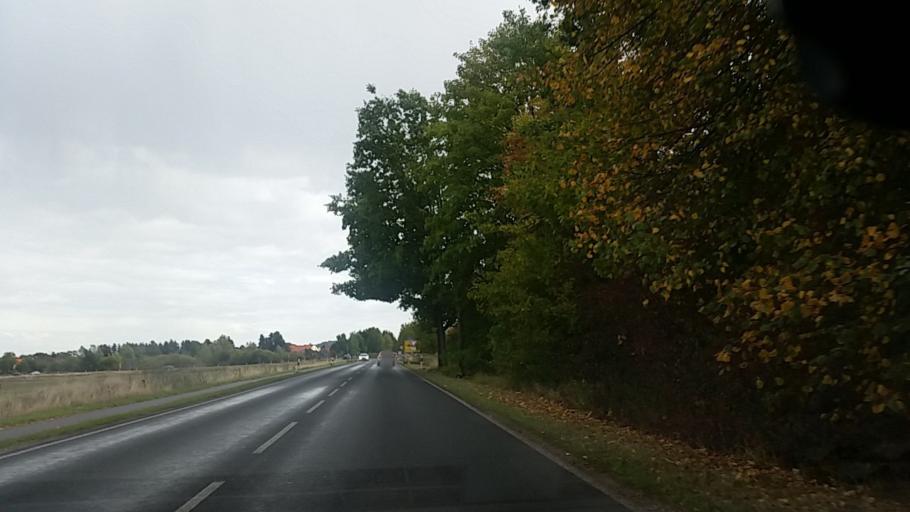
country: DE
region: Lower Saxony
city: Wolfsburg
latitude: 52.3952
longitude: 10.8414
